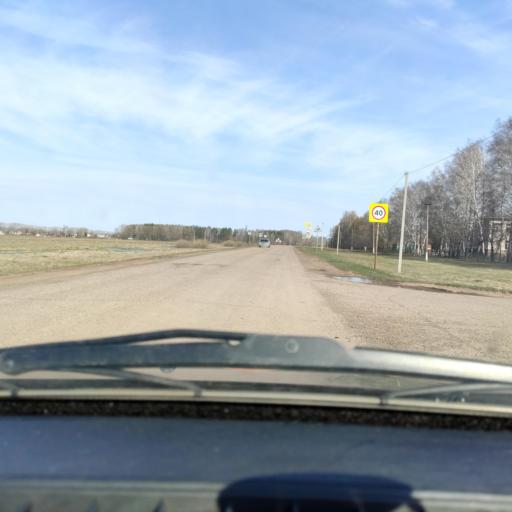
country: RU
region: Bashkortostan
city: Asanovo
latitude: 54.7661
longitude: 55.4868
